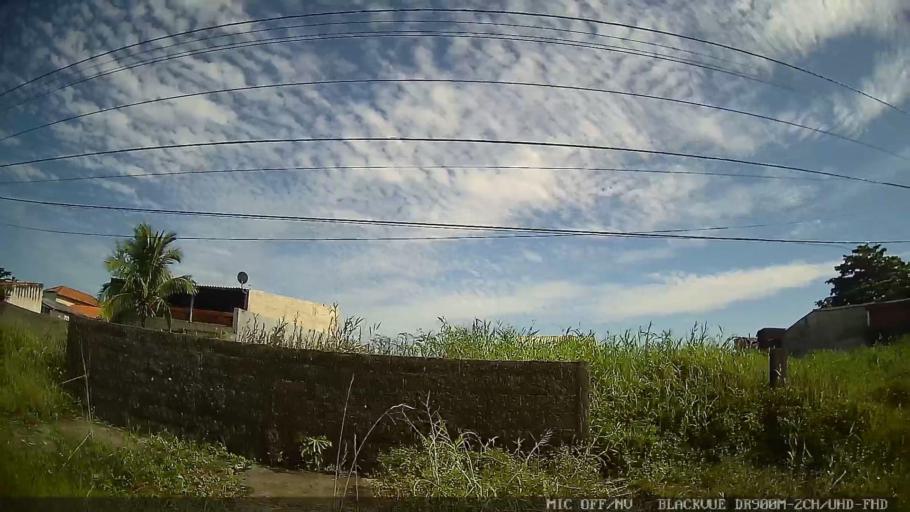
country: BR
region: Sao Paulo
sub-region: Iguape
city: Iguape
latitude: -24.7725
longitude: -47.5888
